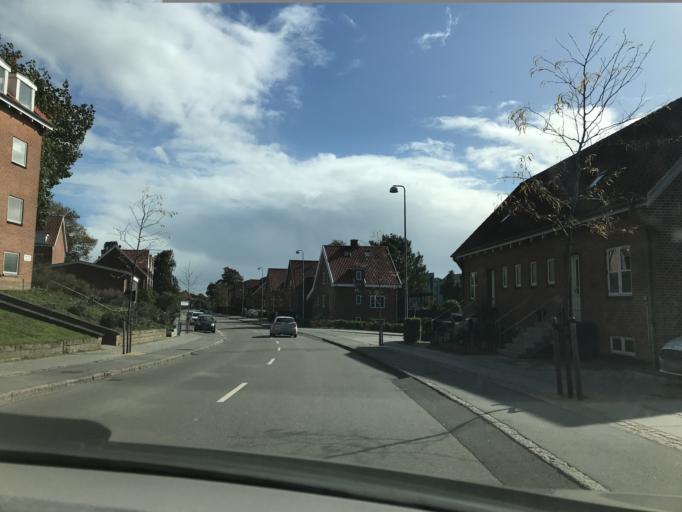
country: DK
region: Central Jutland
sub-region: Skanderborg Kommune
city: Skanderborg
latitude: 56.0347
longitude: 9.9222
